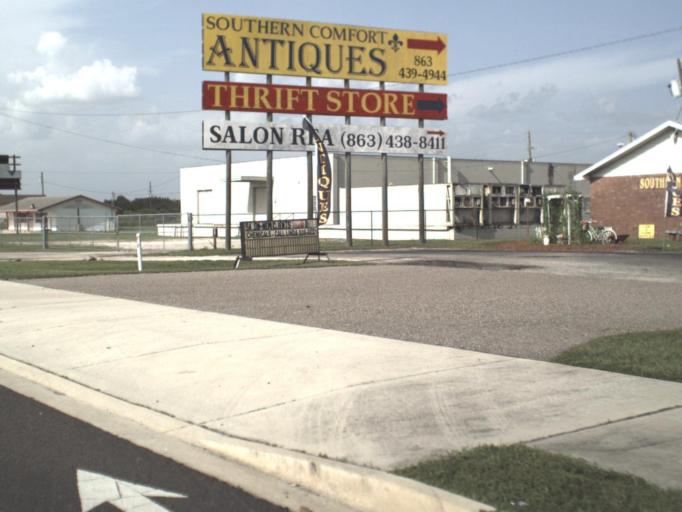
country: US
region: Florida
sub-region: Polk County
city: Lake Hamilton
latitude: 28.0311
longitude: -81.6352
